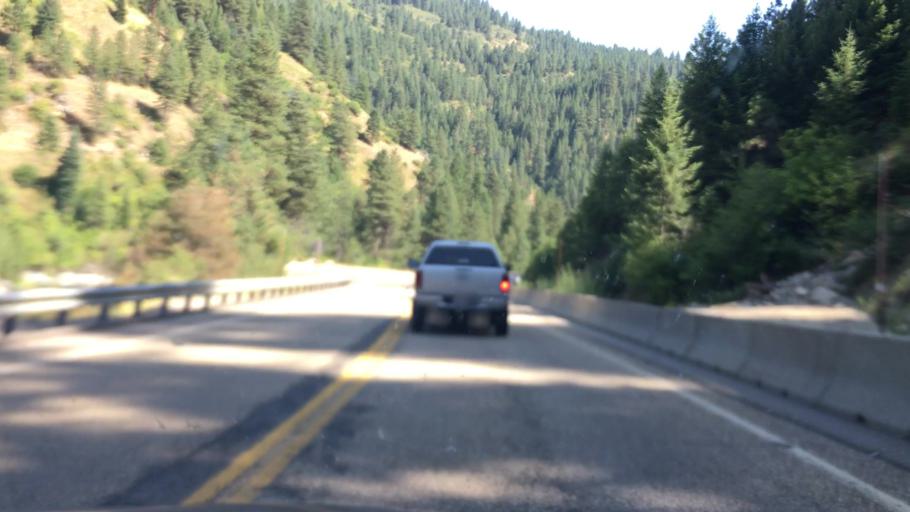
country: US
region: Idaho
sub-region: Valley County
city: Cascade
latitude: 44.1538
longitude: -116.1170
